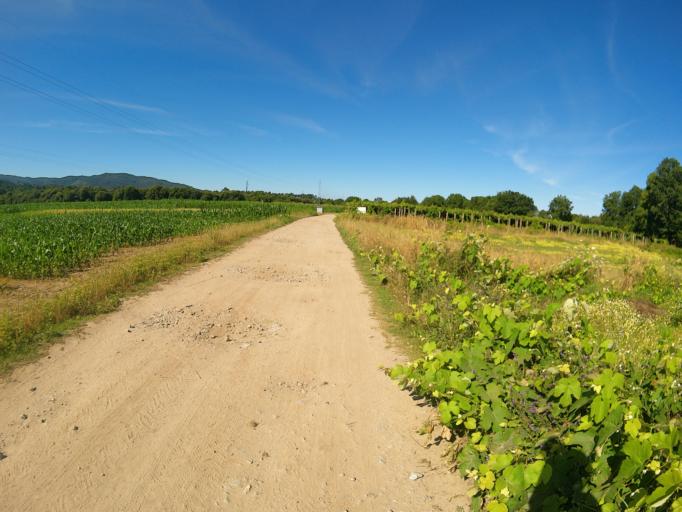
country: PT
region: Viana do Castelo
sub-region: Ponte de Lima
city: Ponte de Lima
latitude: 41.7324
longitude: -8.6599
